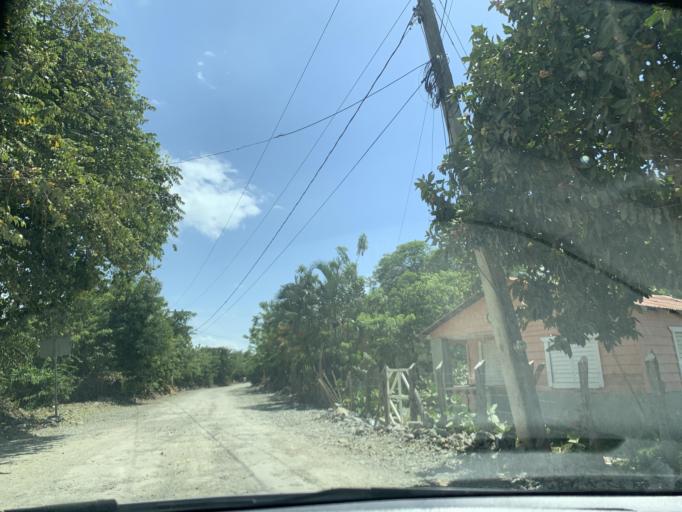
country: DO
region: Puerto Plata
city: Luperon
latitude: 19.8824
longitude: -70.8393
